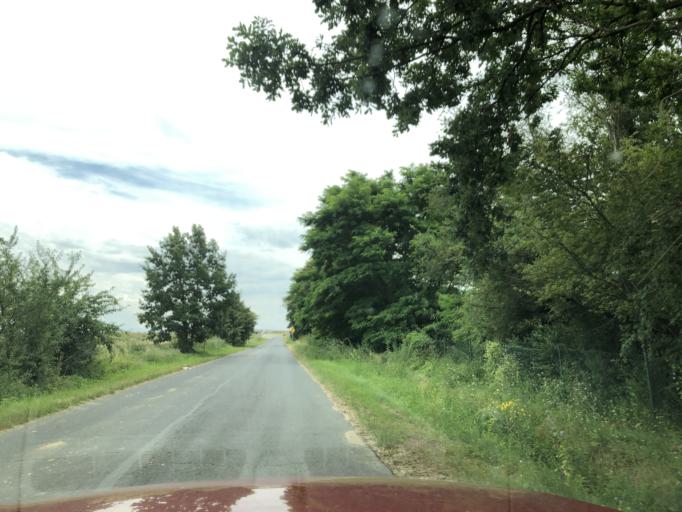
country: PL
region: Lower Silesian Voivodeship
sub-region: Powiat trzebnicki
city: Trzebnica
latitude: 51.3216
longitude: 17.0309
